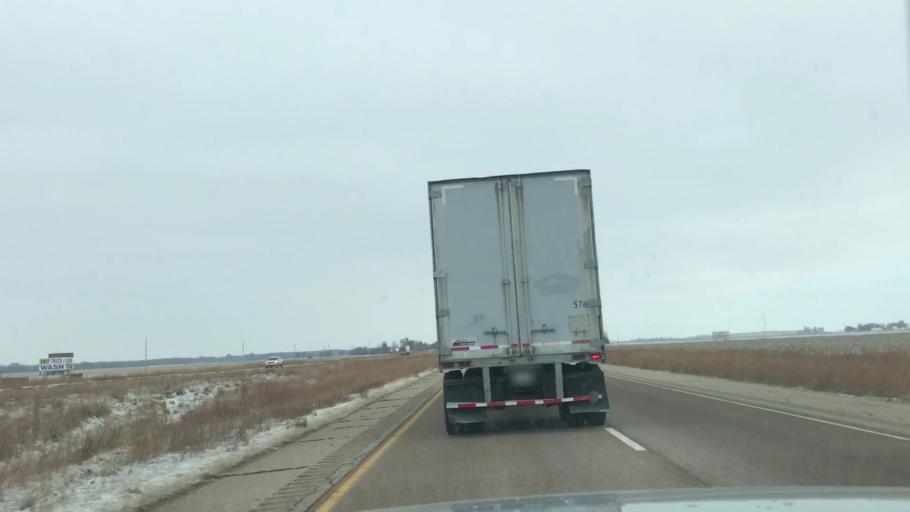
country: US
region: Illinois
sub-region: Montgomery County
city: Raymond
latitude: 39.4016
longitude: -89.6430
